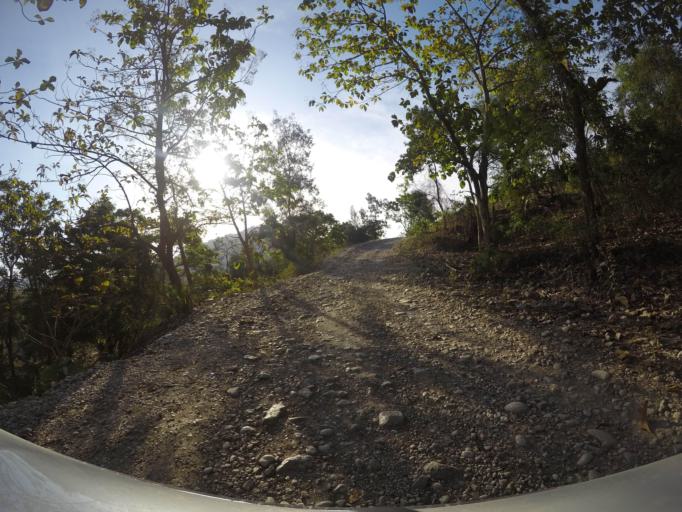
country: TL
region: Viqueque
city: Viqueque
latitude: -8.8007
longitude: 126.5627
